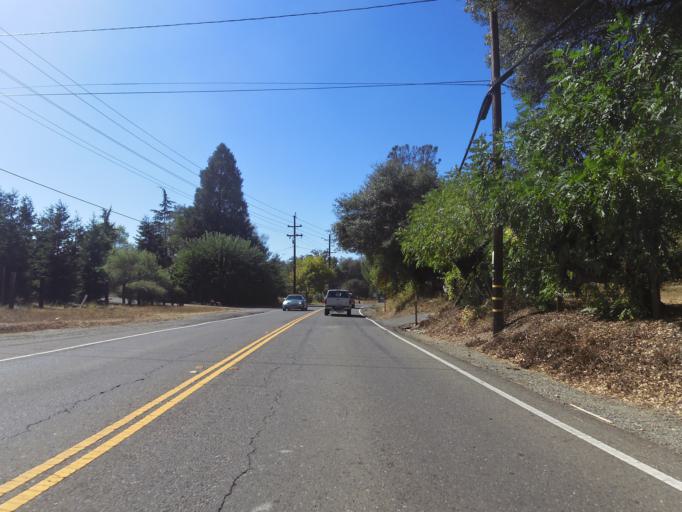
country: US
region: California
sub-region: El Dorado County
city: Deer Park
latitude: 38.6843
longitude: -120.8368
